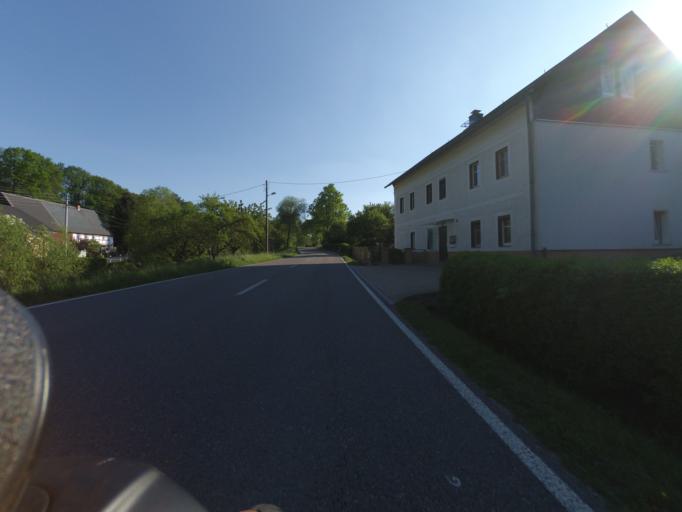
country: DE
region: Saxony
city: Dippoldiswalde
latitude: 50.8866
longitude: 13.6444
